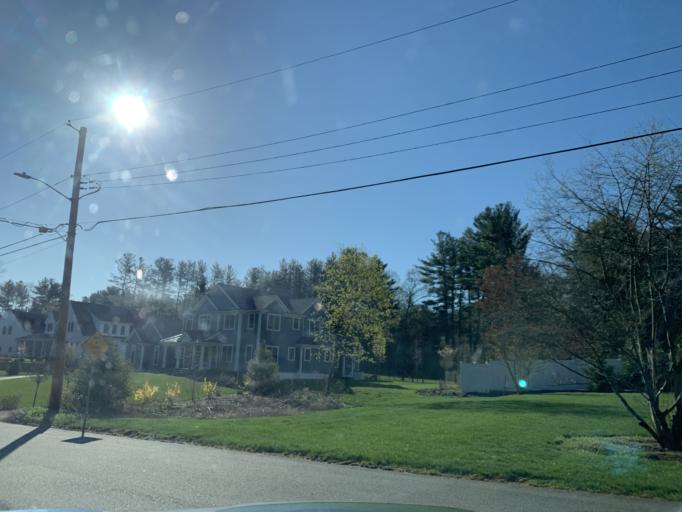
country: US
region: Massachusetts
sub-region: Norfolk County
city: Westwood
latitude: 42.2331
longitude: -71.2090
